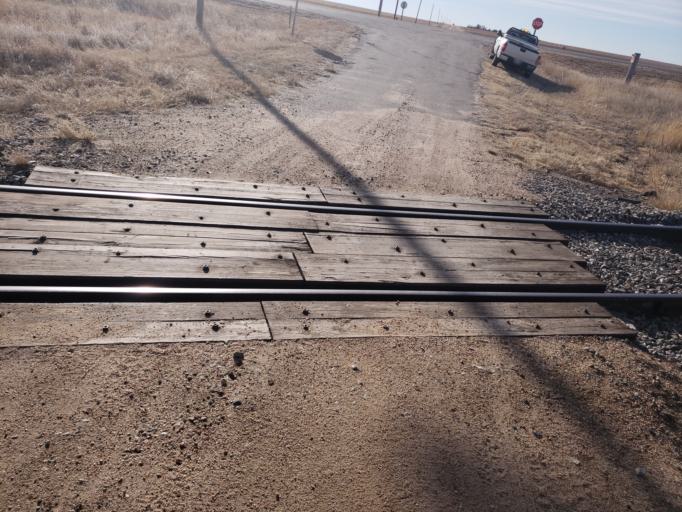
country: US
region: Kansas
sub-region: Ford County
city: Dodge City
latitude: 37.6966
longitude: -100.1607
